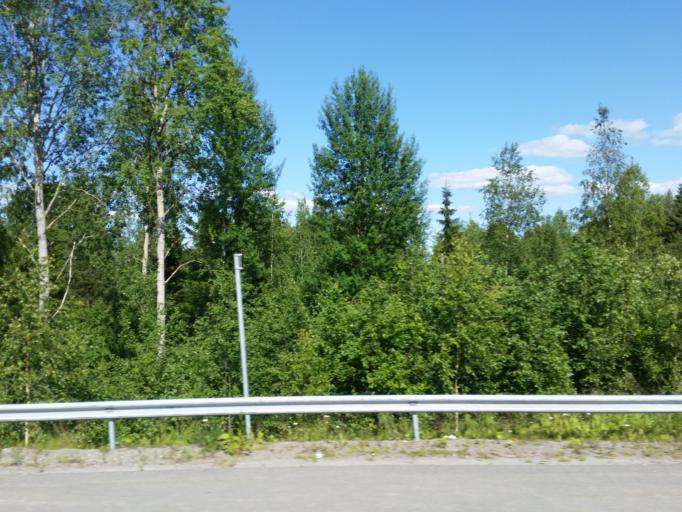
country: FI
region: Northern Savo
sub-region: Varkaus
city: Varkaus
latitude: 62.3057
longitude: 27.8609
